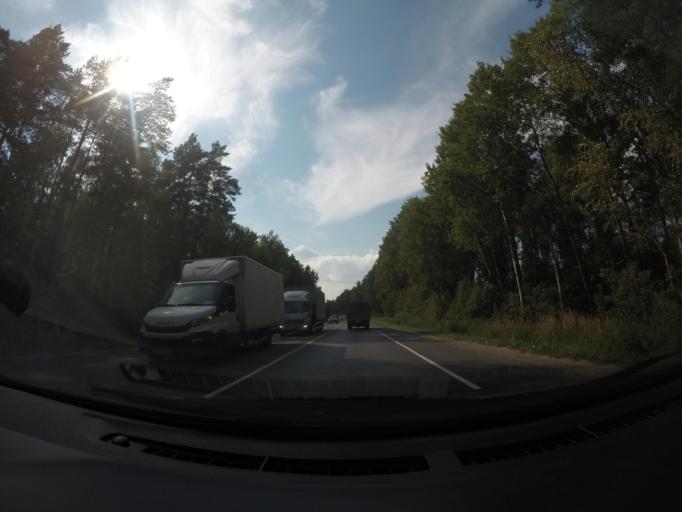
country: RU
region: Moskovskaya
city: Ramenskoye
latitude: 55.6378
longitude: 38.2528
